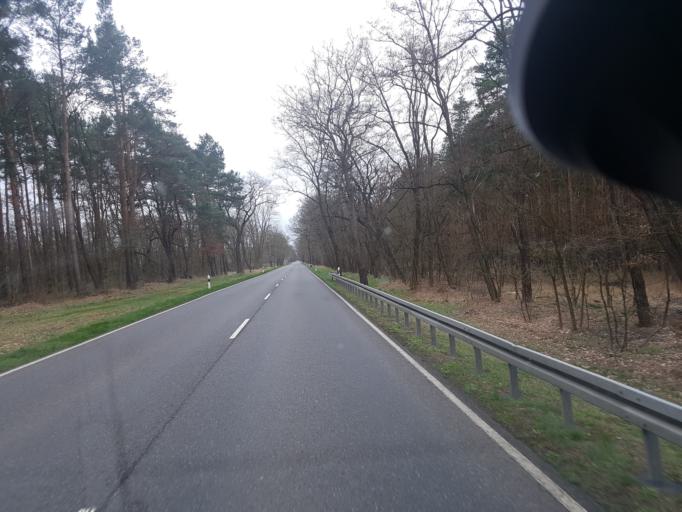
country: DE
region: Brandenburg
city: Schlepzig
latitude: 51.9780
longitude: 13.9599
